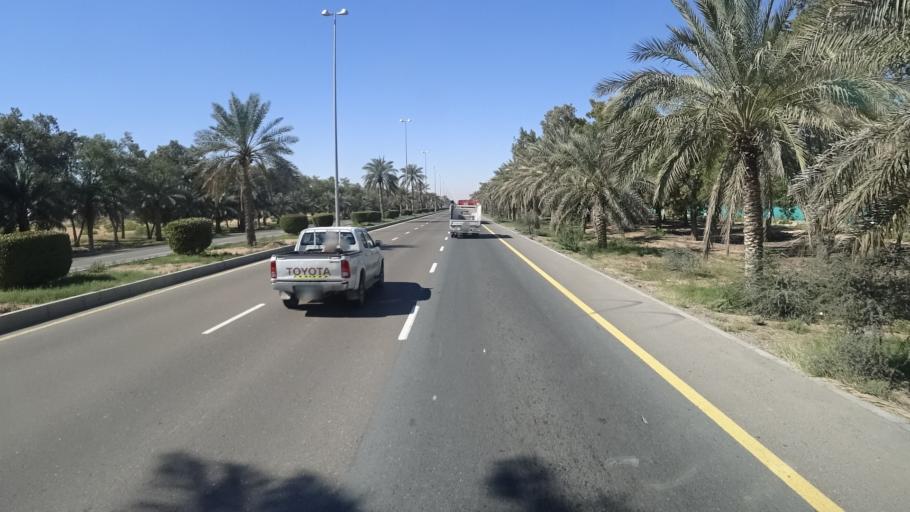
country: AE
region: Abu Dhabi
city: Al Ain
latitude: 24.0852
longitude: 55.6789
